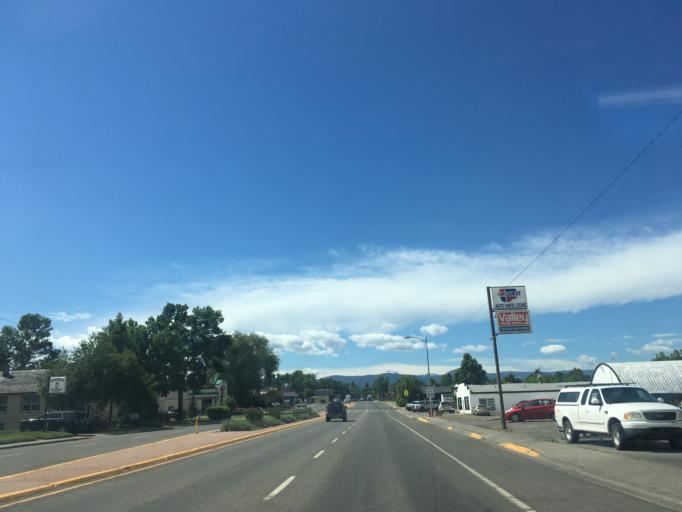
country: US
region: Montana
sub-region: Gallatin County
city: Bozeman
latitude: 45.6844
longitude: -111.0464
